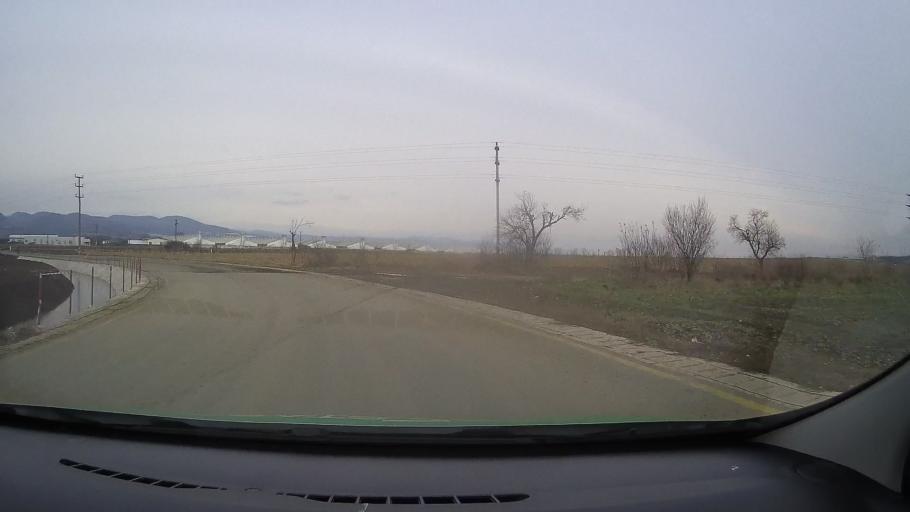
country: RO
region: Hunedoara
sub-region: Comuna Turdas
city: Turdas
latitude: 45.8423
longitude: 23.1376
